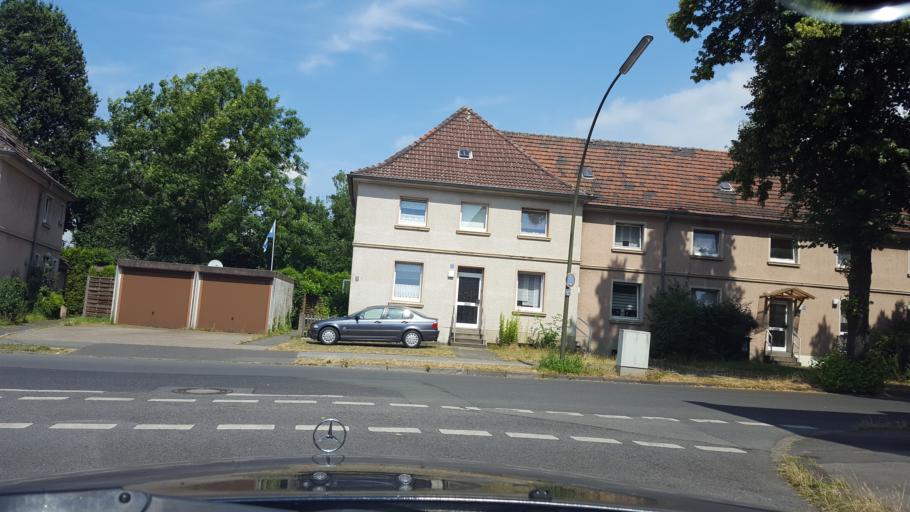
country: DE
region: North Rhine-Westphalia
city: Marl
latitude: 51.6693
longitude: 7.1255
